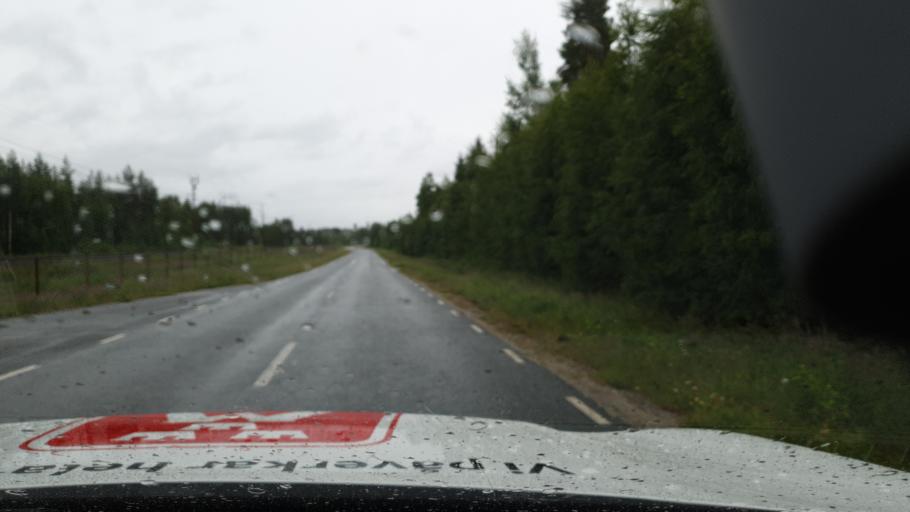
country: SE
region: Vaesterbotten
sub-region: Vindelns Kommun
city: Vindeln
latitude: 64.4466
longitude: 19.7495
